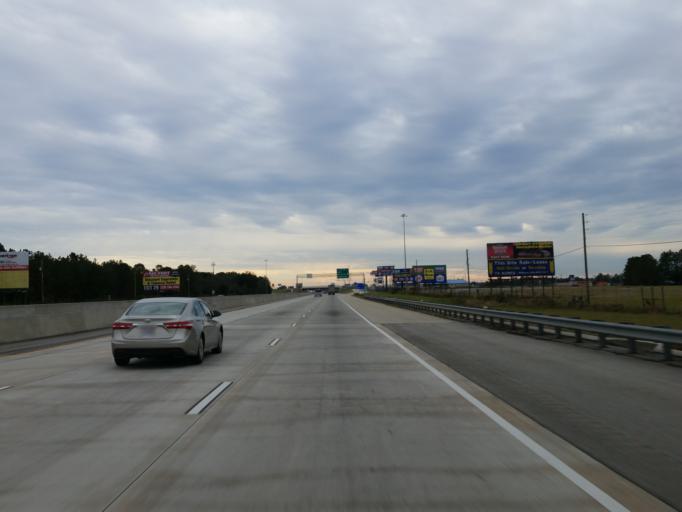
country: US
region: Georgia
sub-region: Cook County
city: Adel
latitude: 31.1443
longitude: -83.4422
